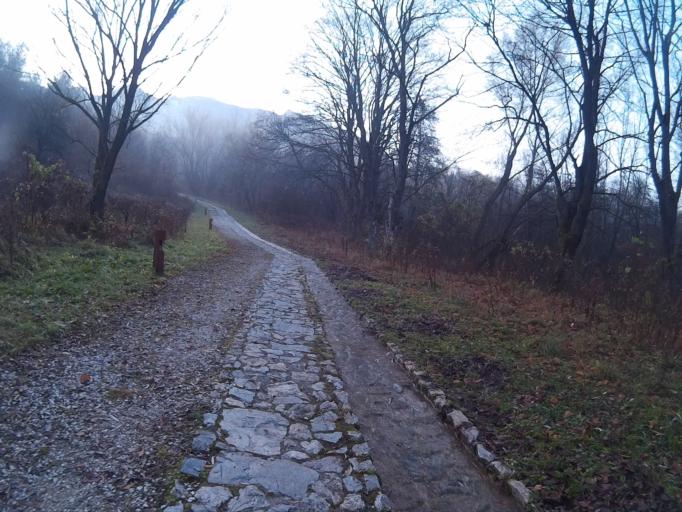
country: HU
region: Heves
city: Belapatfalva
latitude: 48.0505
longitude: 20.3615
